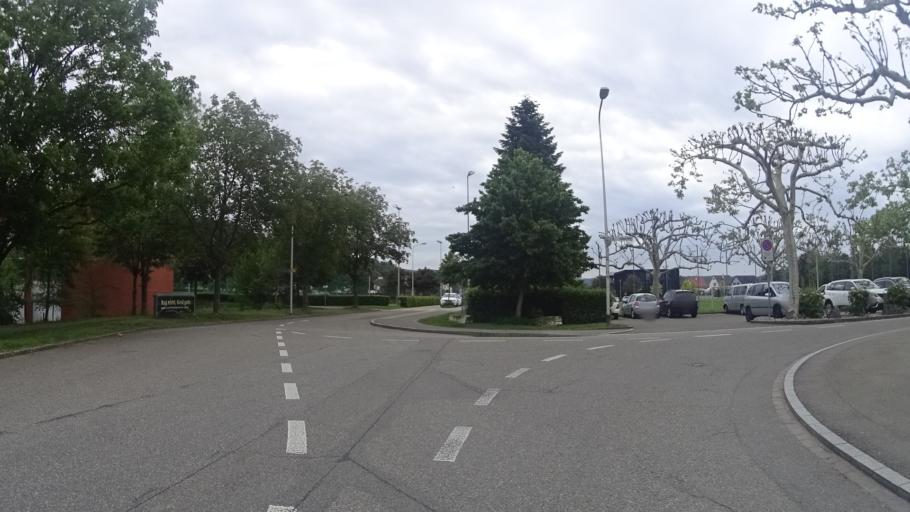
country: CH
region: Aargau
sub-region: Bezirk Baden
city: Untersiggenthal
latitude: 47.4997
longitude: 8.2574
